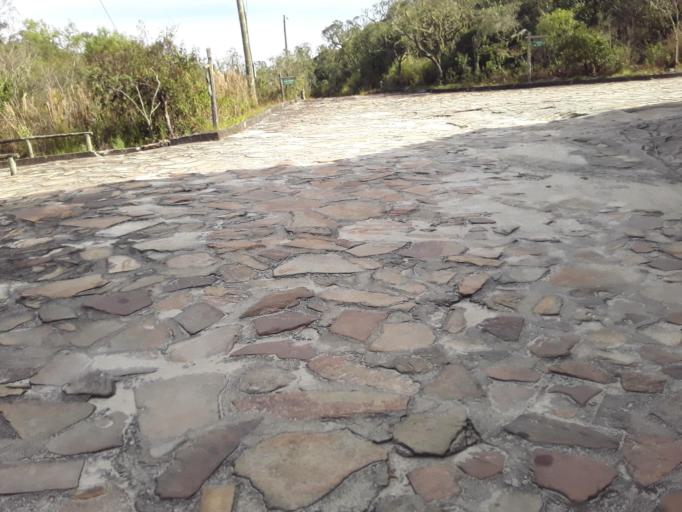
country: BR
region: Minas Gerais
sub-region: Lima Duarte
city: Lima Duarte
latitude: -21.7124
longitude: -43.8967
